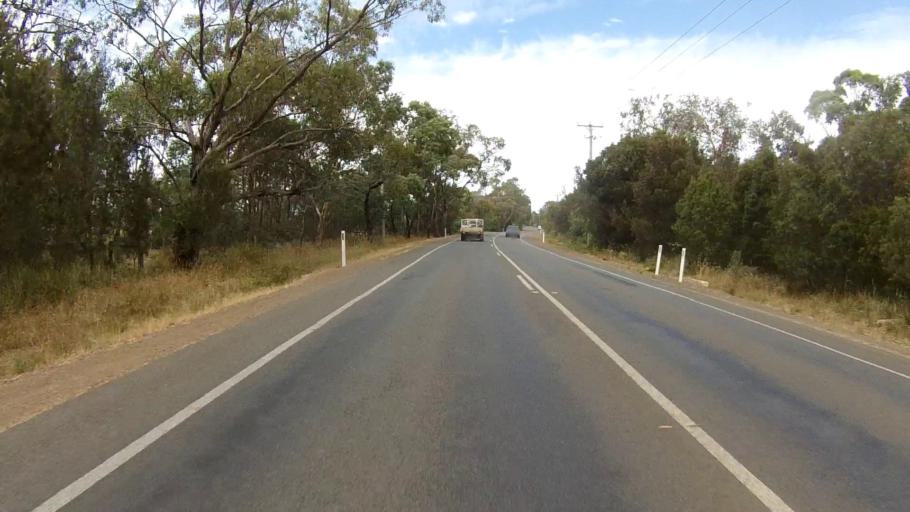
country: AU
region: Tasmania
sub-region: Clarence
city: Sandford
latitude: -42.9407
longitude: 147.4969
